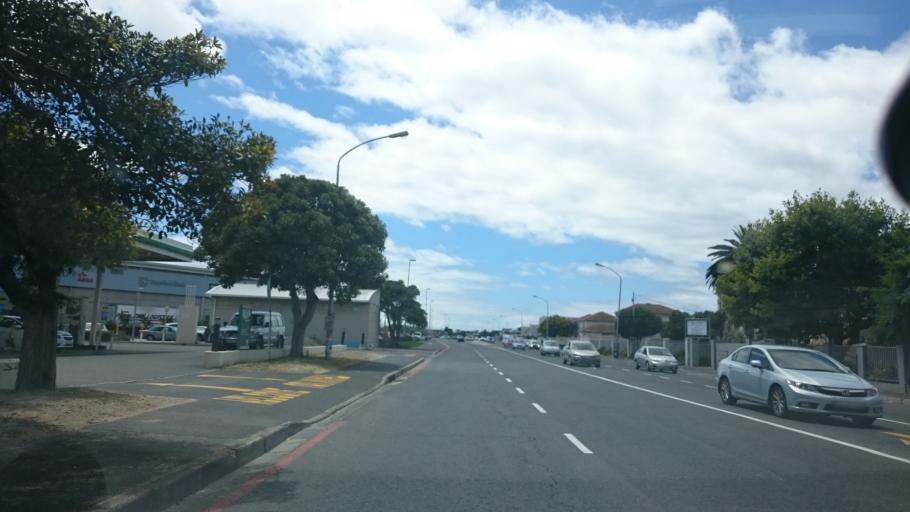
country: ZA
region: Western Cape
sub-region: City of Cape Town
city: Bergvliet
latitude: -34.0649
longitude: 18.4518
